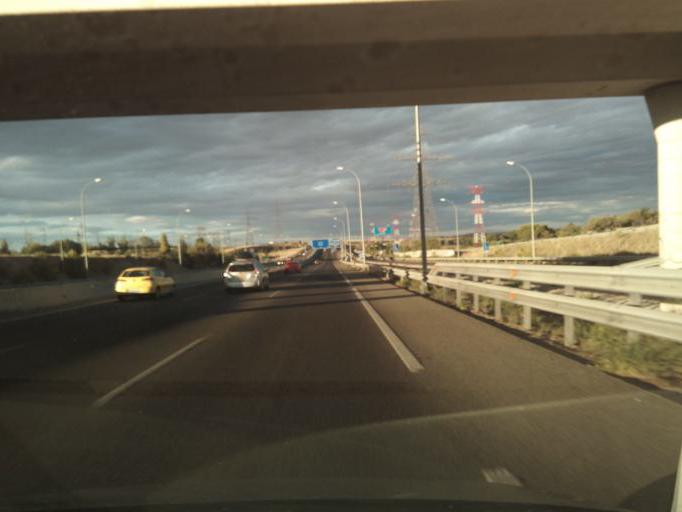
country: ES
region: Madrid
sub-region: Provincia de Madrid
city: San Sebastian de los Reyes
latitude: 40.5568
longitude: -3.6027
